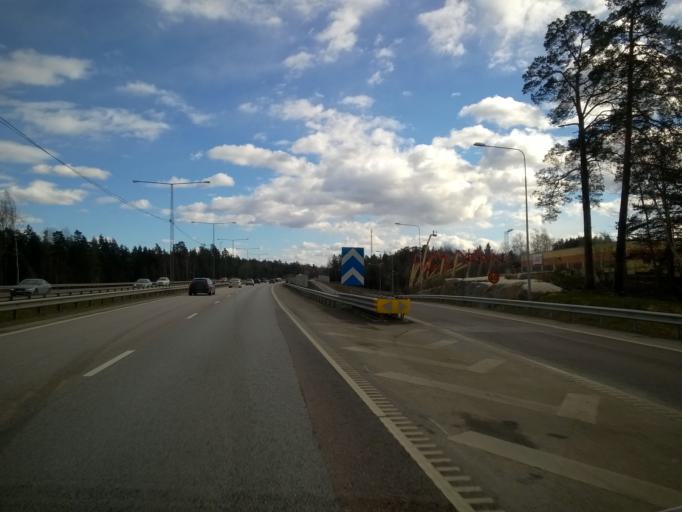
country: SE
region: Stockholm
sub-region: Jarfalla Kommun
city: Jakobsberg
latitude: 59.4514
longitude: 17.8360
